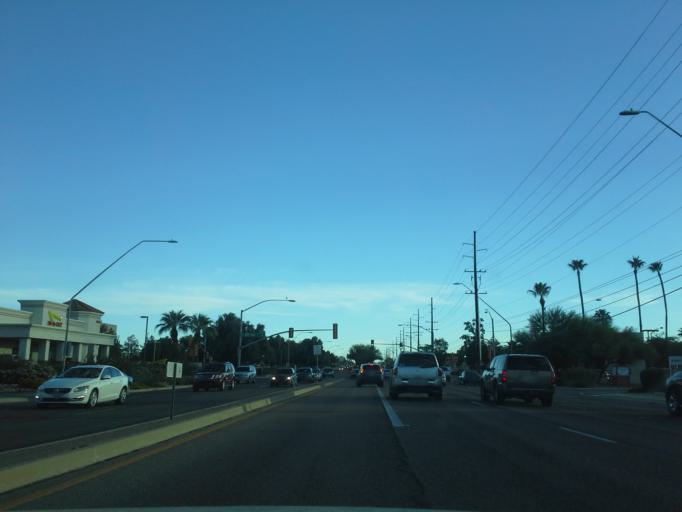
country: US
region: Arizona
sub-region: Pima County
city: Flowing Wells
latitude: 32.2912
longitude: -110.9783
